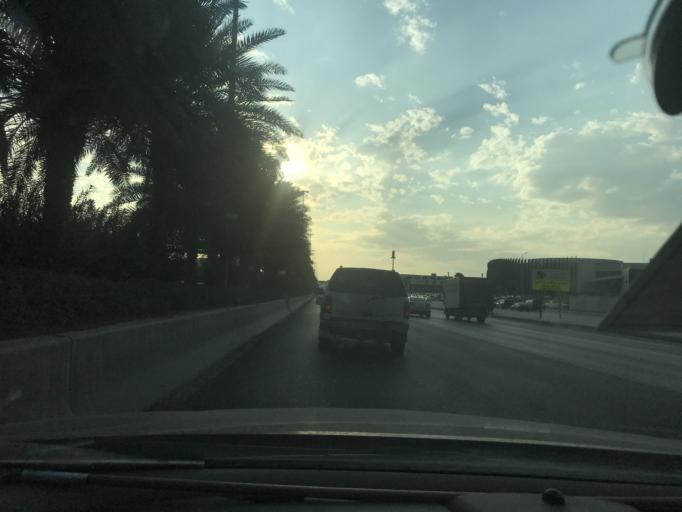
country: SA
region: Ar Riyad
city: Riyadh
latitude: 24.7553
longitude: 46.6334
